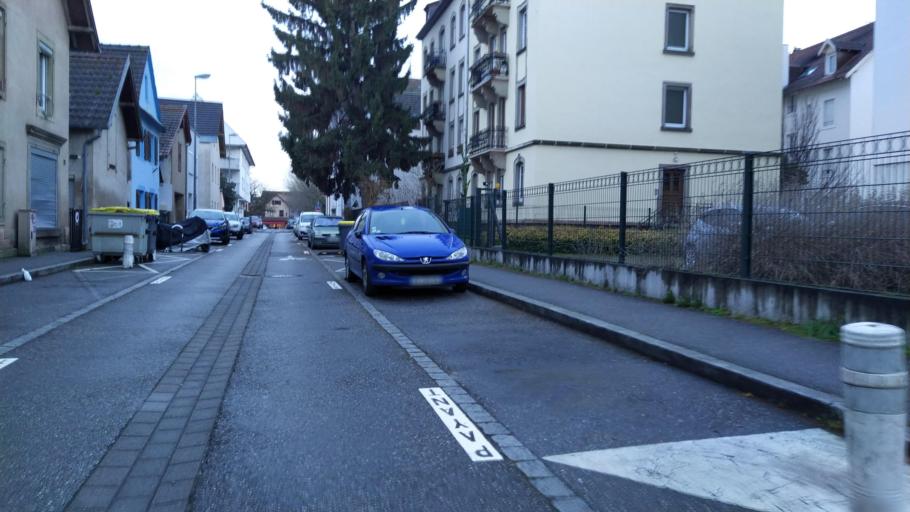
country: FR
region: Alsace
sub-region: Departement du Bas-Rhin
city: Schiltigheim
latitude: 48.6096
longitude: 7.7518
